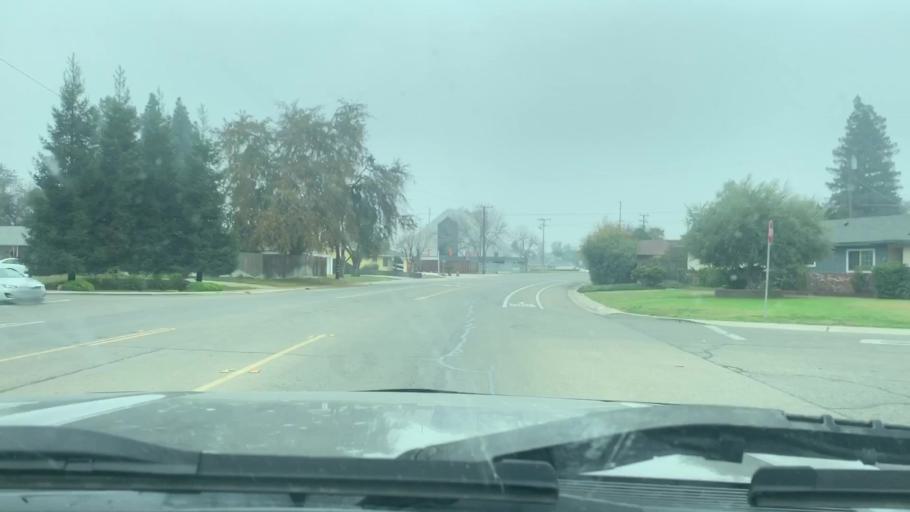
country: US
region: California
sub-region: Tulare County
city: Visalia
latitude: 36.3148
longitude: -119.3234
